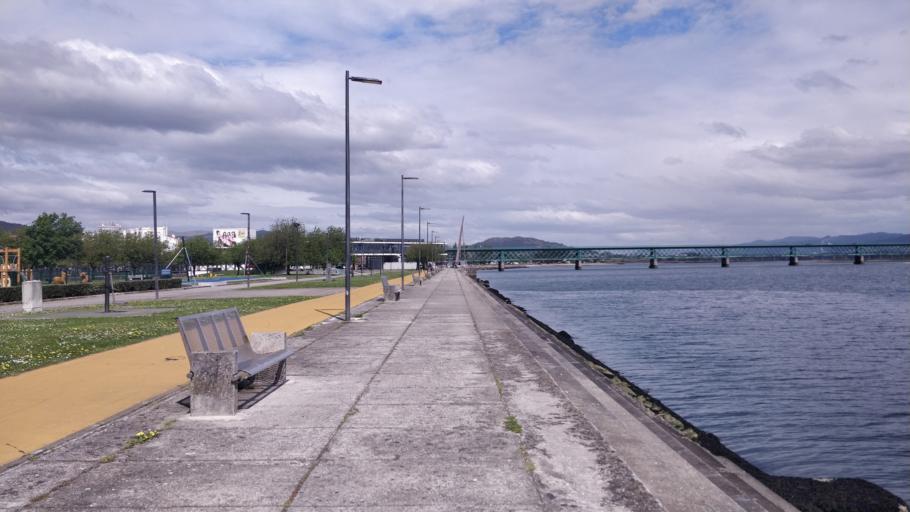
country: PT
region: Viana do Castelo
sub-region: Viana do Castelo
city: Viana do Castelo
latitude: 41.6916
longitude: -8.8252
